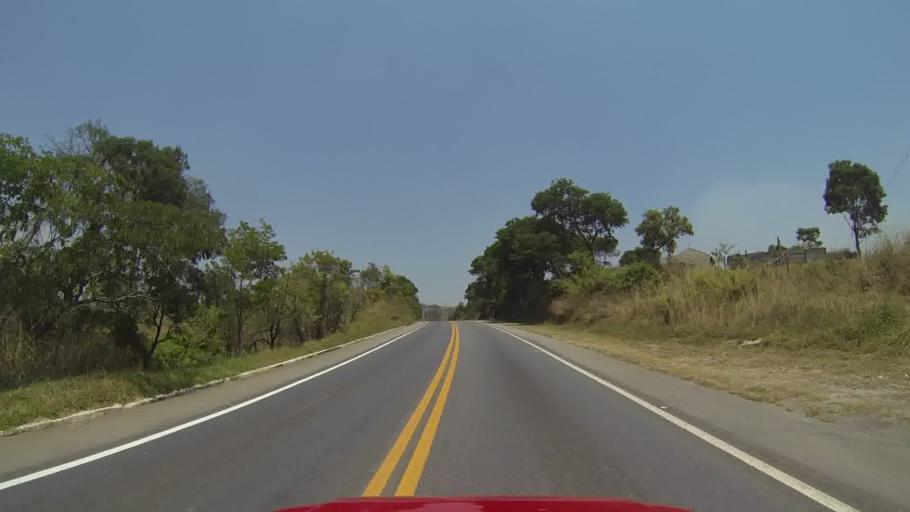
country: BR
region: Minas Gerais
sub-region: Itapecerica
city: Itapecerica
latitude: -20.3299
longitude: -45.2285
